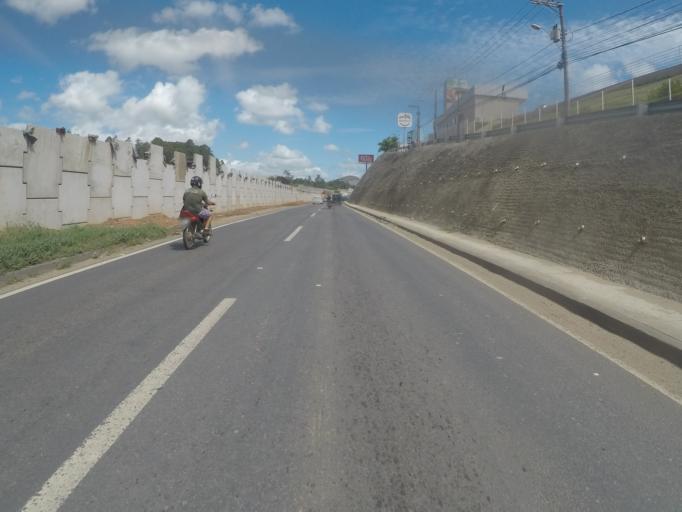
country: BR
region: Espirito Santo
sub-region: Viana
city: Viana
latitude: -20.3562
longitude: -40.4185
